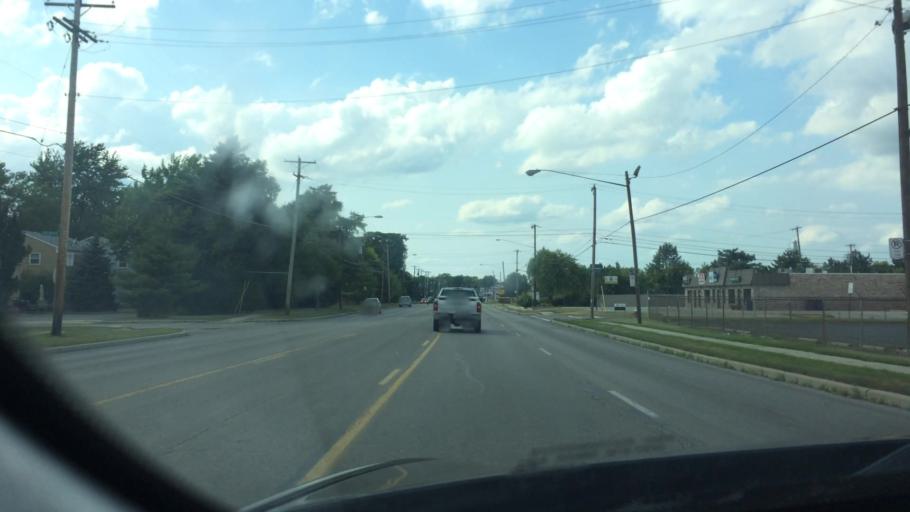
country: US
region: Ohio
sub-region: Wood County
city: Perrysburg
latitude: 41.5974
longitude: -83.6216
